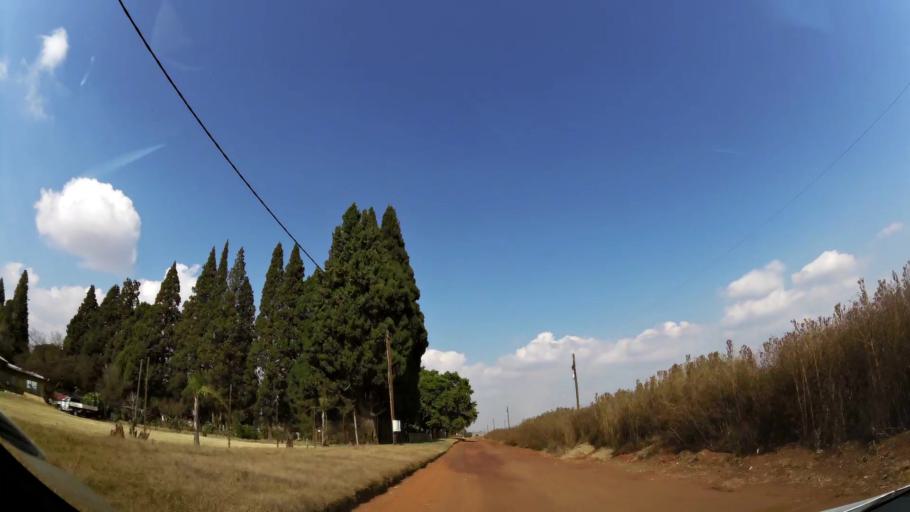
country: ZA
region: Gauteng
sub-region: Ekurhuleni Metropolitan Municipality
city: Springs
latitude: -26.1901
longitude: 28.5331
